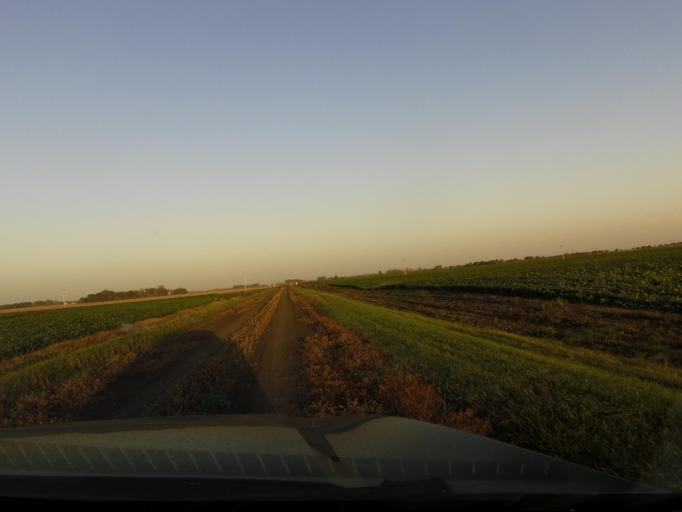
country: US
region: North Dakota
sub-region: Walsh County
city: Grafton
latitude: 48.3830
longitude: -97.2365
